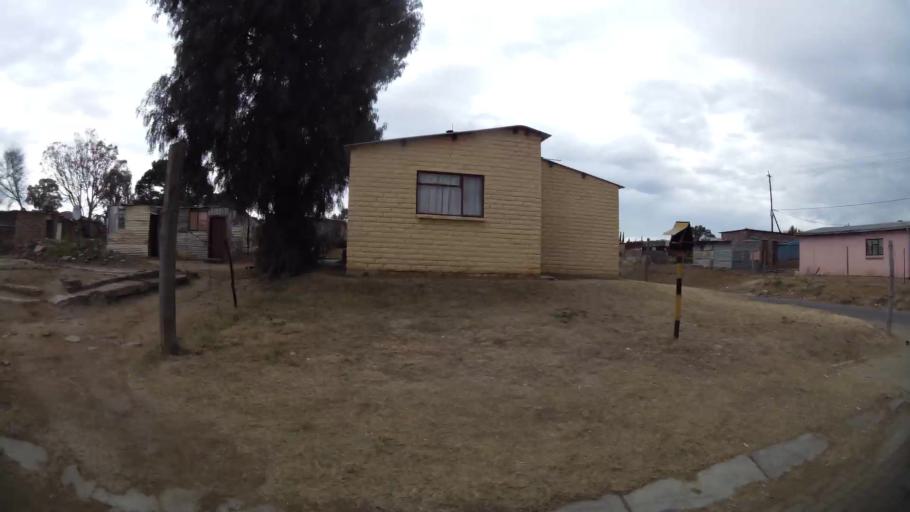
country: ZA
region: Orange Free State
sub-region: Fezile Dabi District Municipality
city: Kroonstad
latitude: -27.6461
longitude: 27.2182
